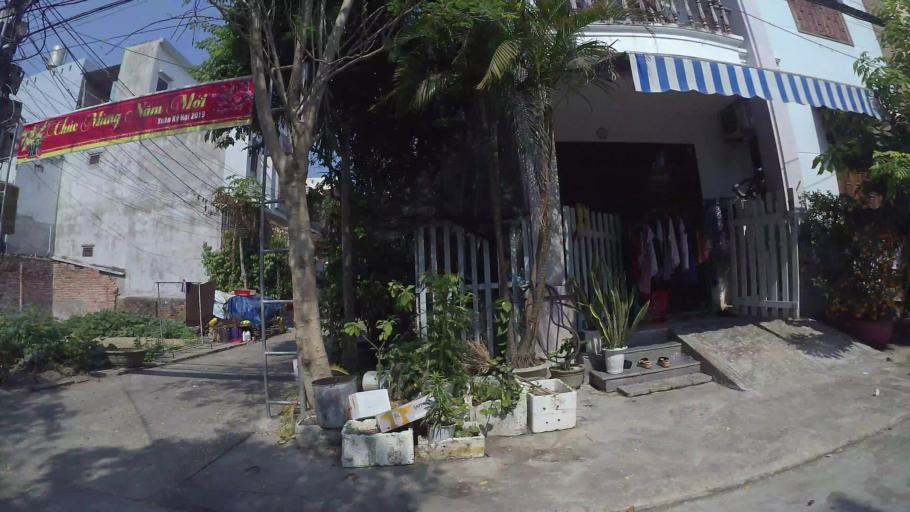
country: VN
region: Da Nang
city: Ngu Hanh Son
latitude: 16.0218
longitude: 108.2520
